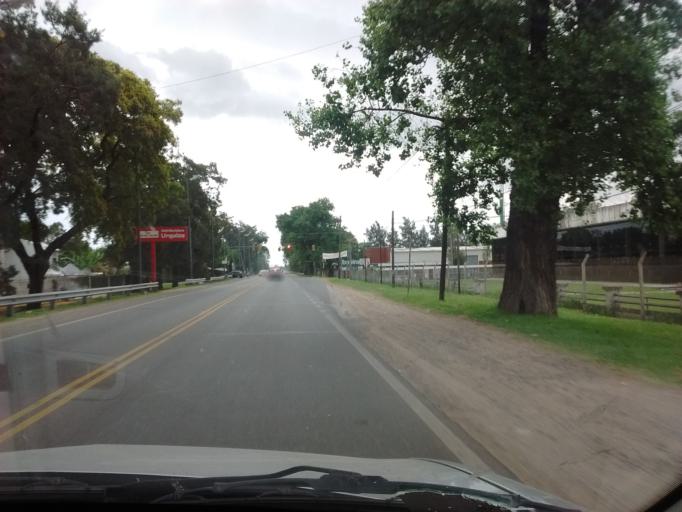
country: AR
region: Santa Fe
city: Funes
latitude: -32.9261
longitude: -60.7556
